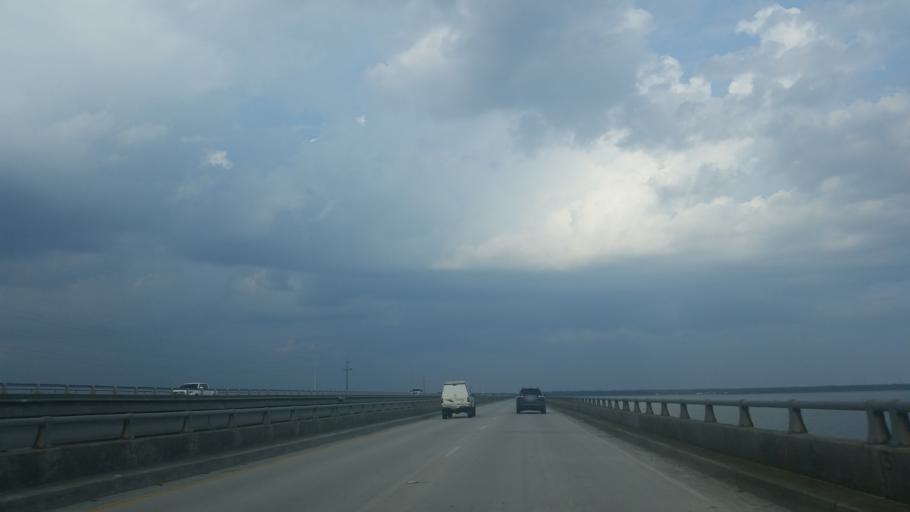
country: US
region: North Carolina
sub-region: Dare County
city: Southern Shores
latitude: 36.0819
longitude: -75.7843
